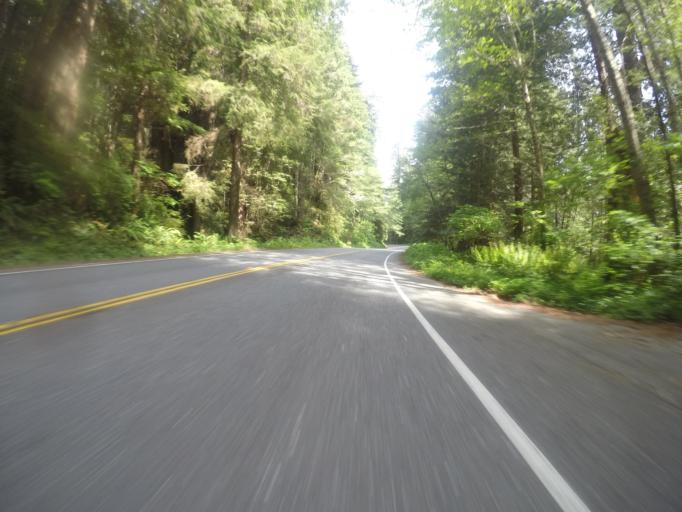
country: US
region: California
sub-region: Del Norte County
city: Bertsch-Oceanview
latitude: 41.4547
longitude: -124.0437
